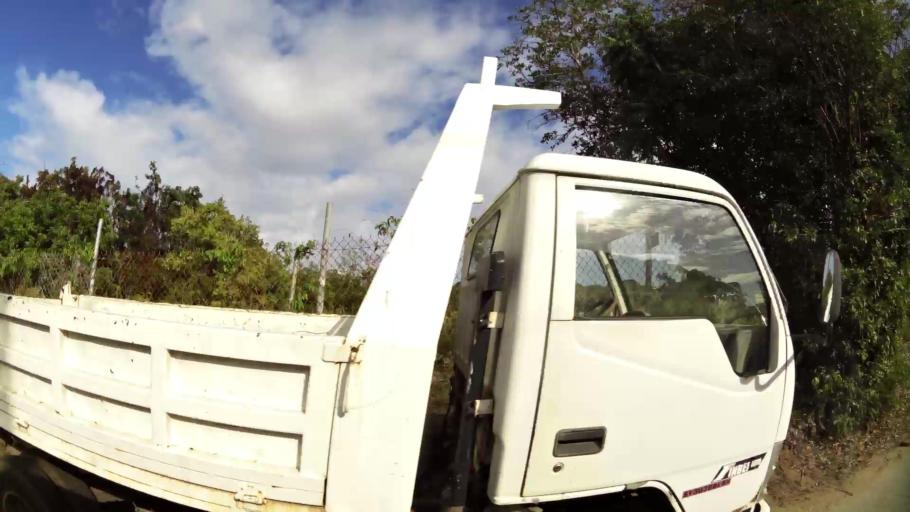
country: VG
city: Tortola
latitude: 18.4384
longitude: -64.4348
